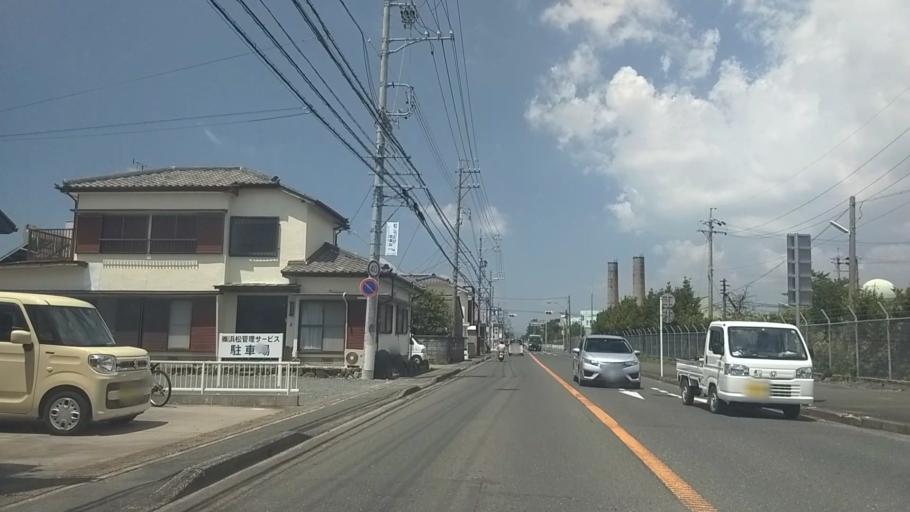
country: JP
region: Shizuoka
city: Hamamatsu
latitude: 34.7400
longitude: 137.6965
